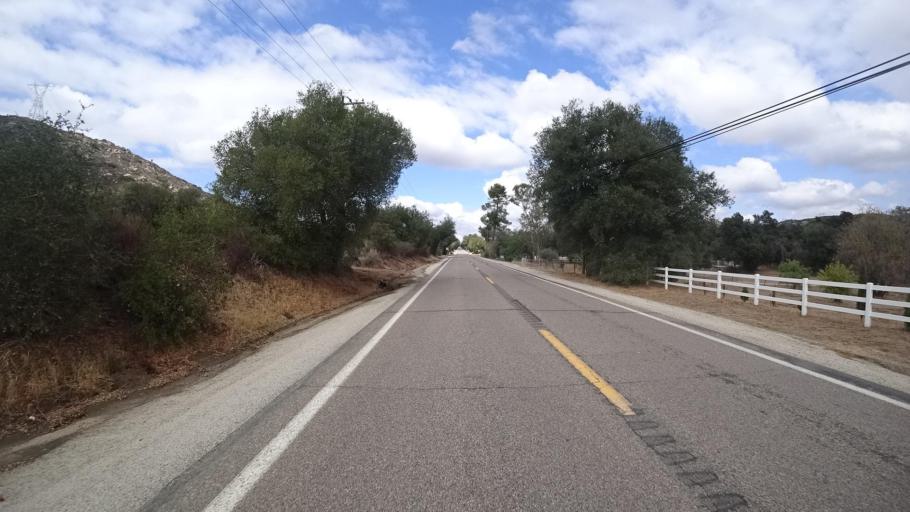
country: US
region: California
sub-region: San Diego County
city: Campo
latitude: 32.6587
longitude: -116.4878
